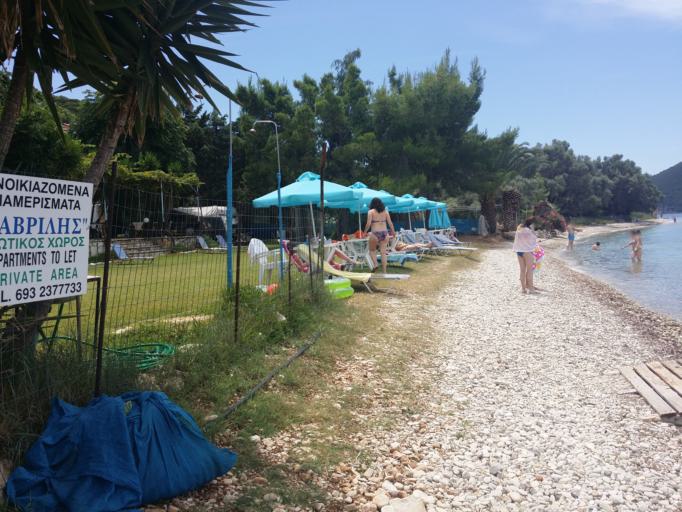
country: GR
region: Ionian Islands
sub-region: Lefkada
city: Nidri
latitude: 38.6463
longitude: 20.7382
